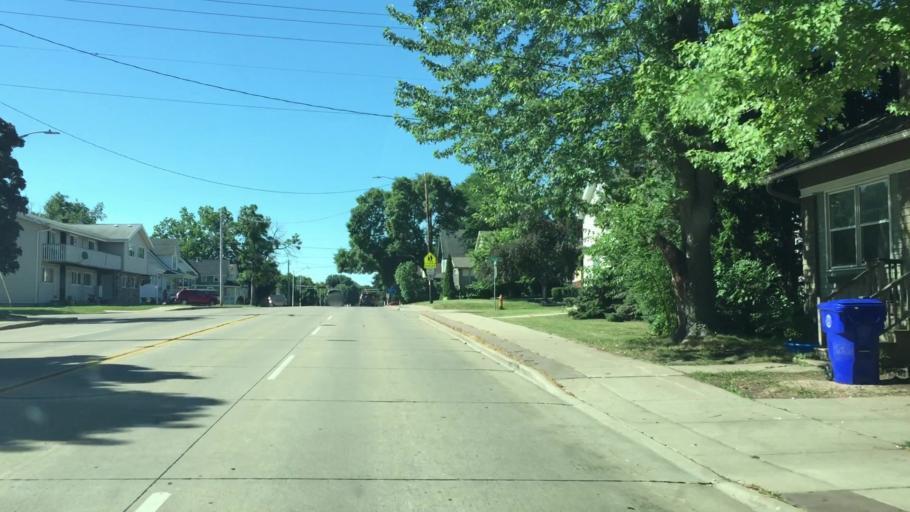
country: US
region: Wisconsin
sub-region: Outagamie County
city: Appleton
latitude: 44.2568
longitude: -88.4154
